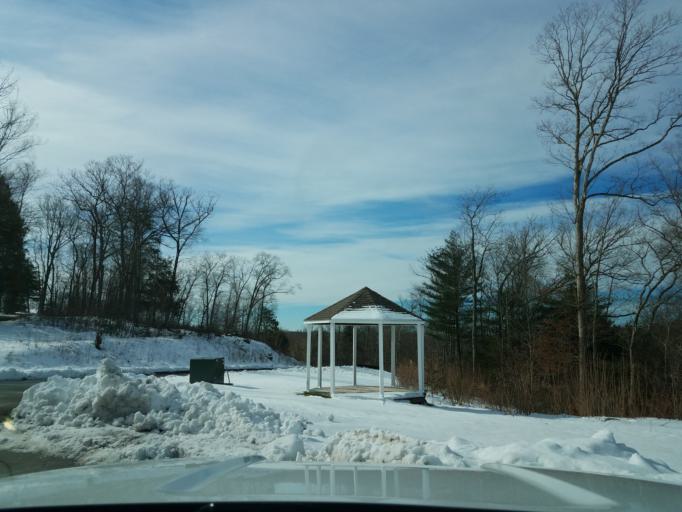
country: US
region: Connecticut
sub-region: New Haven County
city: Guilford
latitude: 41.3542
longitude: -72.6701
